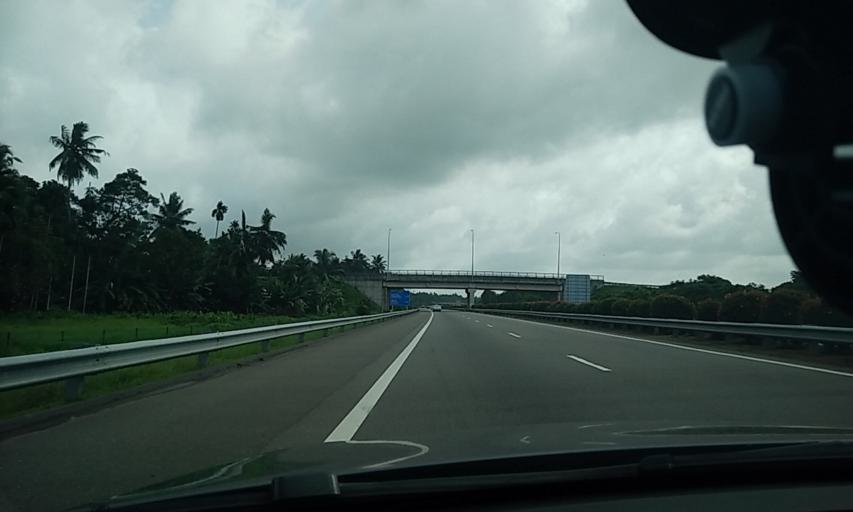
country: LK
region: Western
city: Homagama
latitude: 6.8508
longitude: 79.9785
